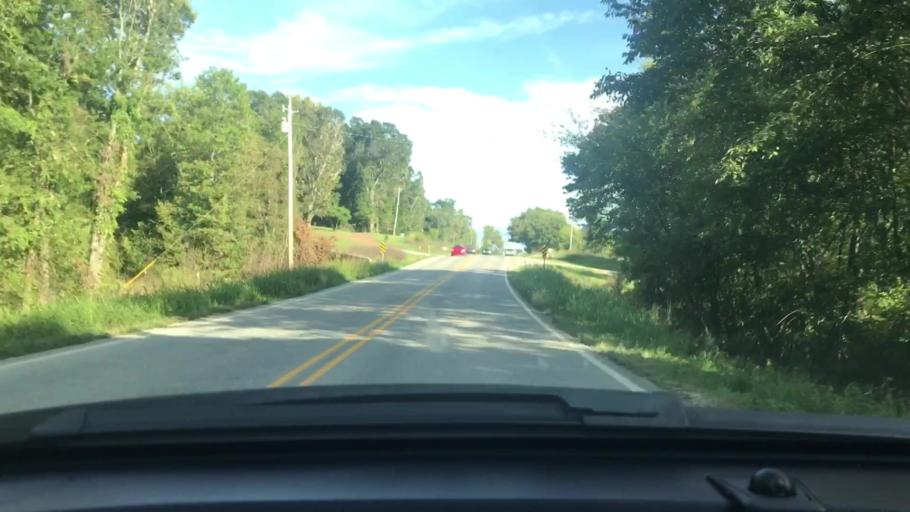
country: US
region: Arkansas
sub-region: Sharp County
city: Cherokee Village
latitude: 36.3076
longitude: -91.4554
